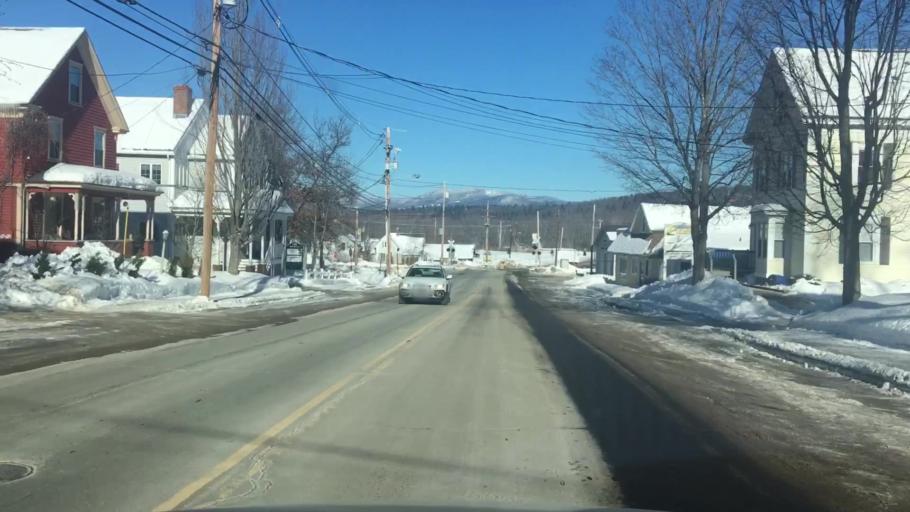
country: US
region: Maine
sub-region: Oxford County
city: Bethel
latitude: 44.4098
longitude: -70.7883
